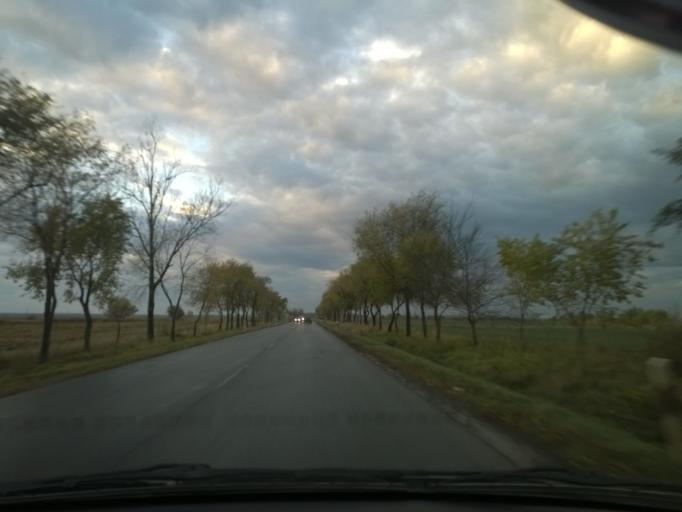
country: HU
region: Bacs-Kiskun
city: Solt
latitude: 46.8451
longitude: 19.0029
